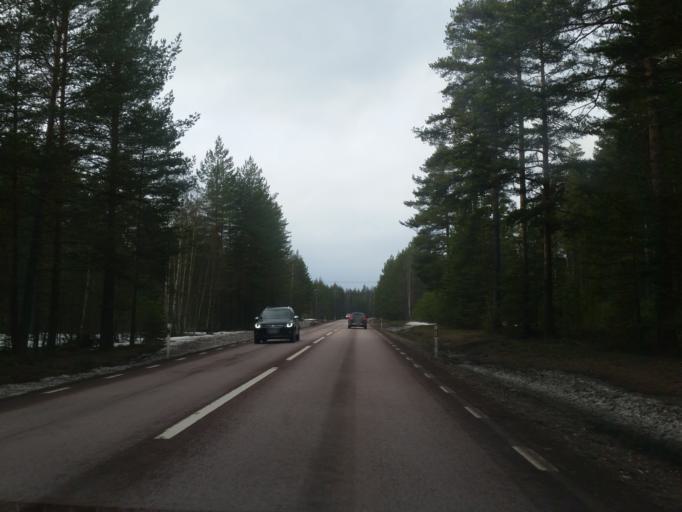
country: SE
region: Dalarna
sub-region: Mora Kommun
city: Mora
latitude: 61.0479
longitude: 14.4735
